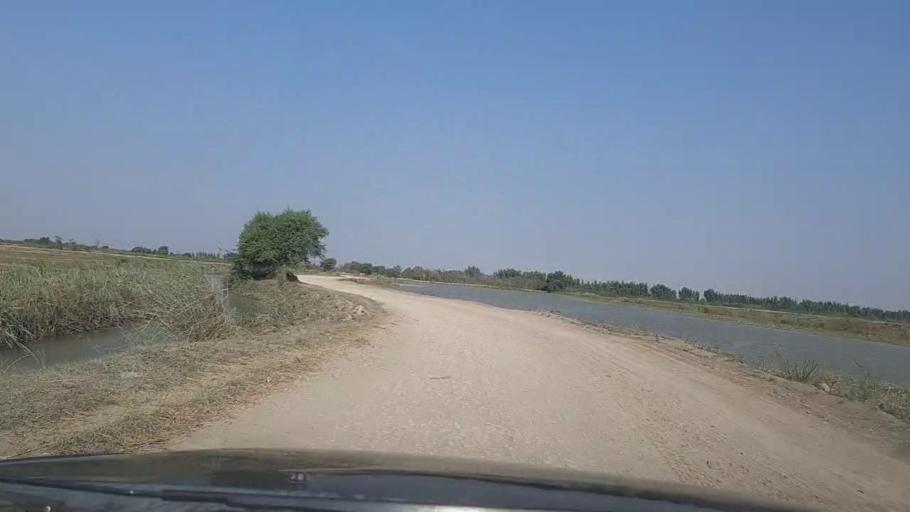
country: PK
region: Sindh
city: Thatta
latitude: 24.6275
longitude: 67.8139
